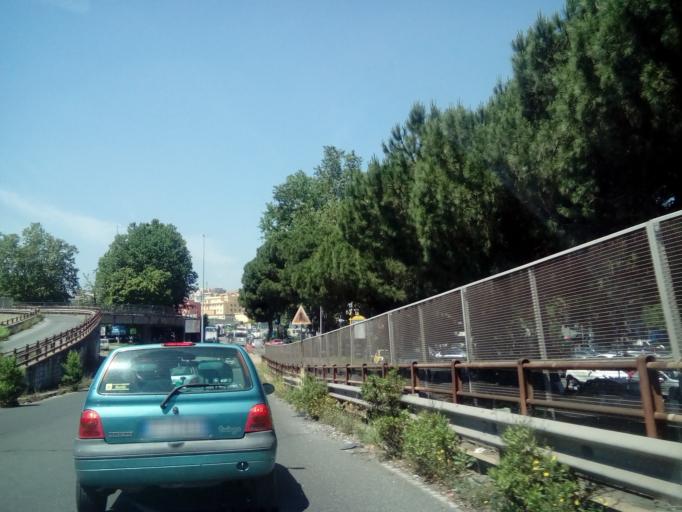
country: IT
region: Latium
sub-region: Citta metropolitana di Roma Capitale
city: Rome
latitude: 41.9087
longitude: 12.5281
